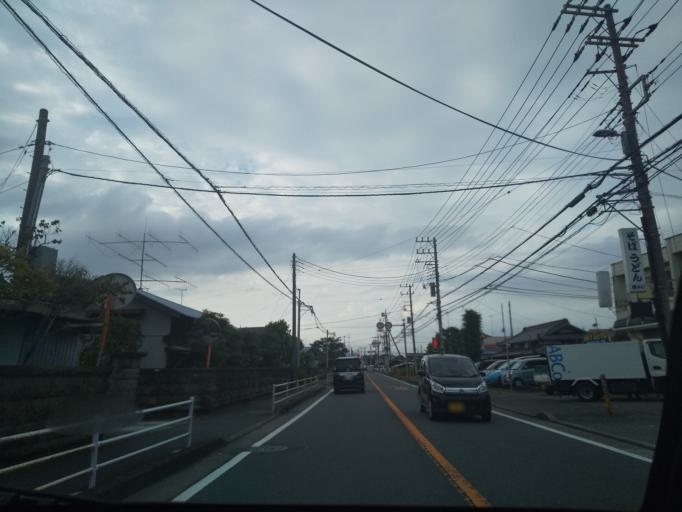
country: JP
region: Kanagawa
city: Zama
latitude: 35.4680
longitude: 139.3887
